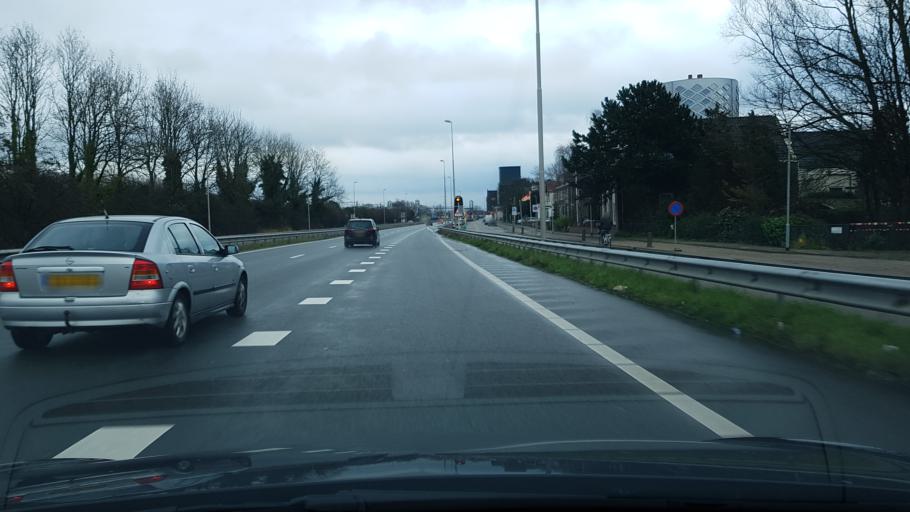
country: NL
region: North Holland
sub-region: Gemeente Haarlemmermeer
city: Hoofddorp
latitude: 52.3863
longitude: 4.7399
